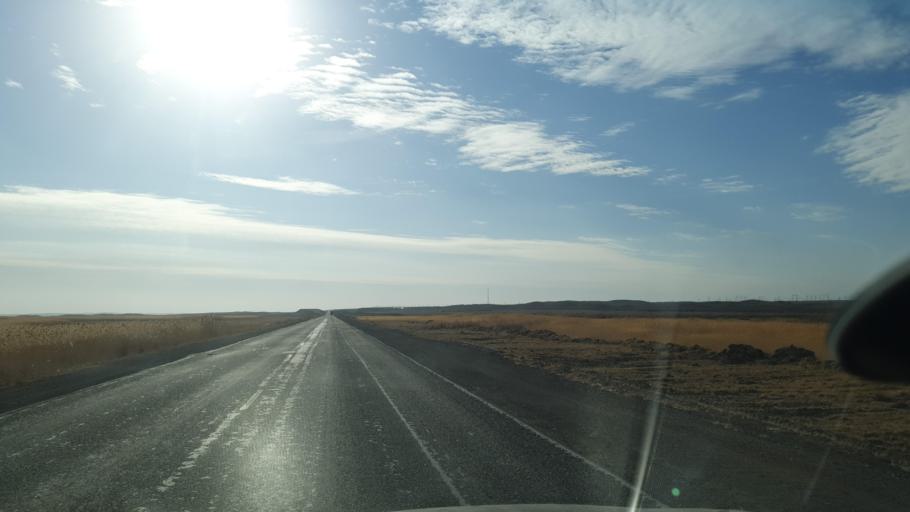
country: KZ
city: Priozersk
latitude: 45.8372
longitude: 73.4554
